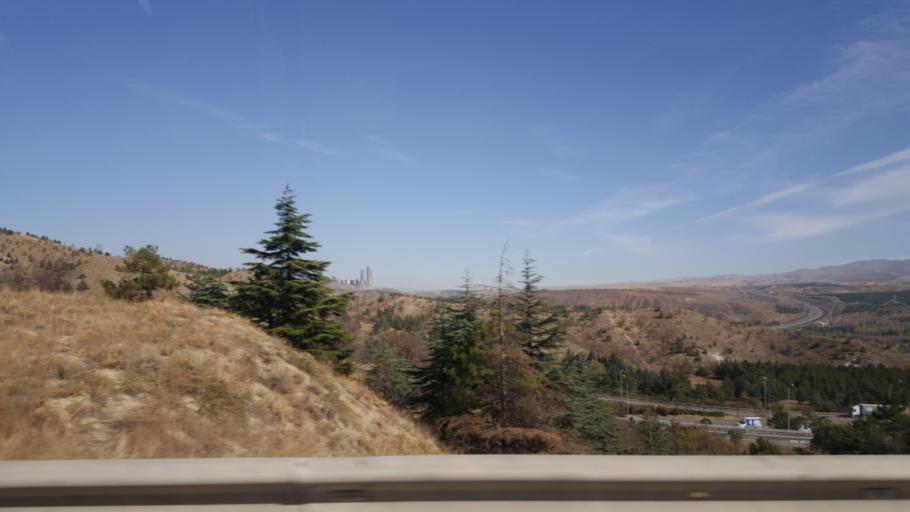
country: TR
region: Ankara
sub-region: Goelbasi
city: Golbasi
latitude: 39.8122
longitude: 32.7986
